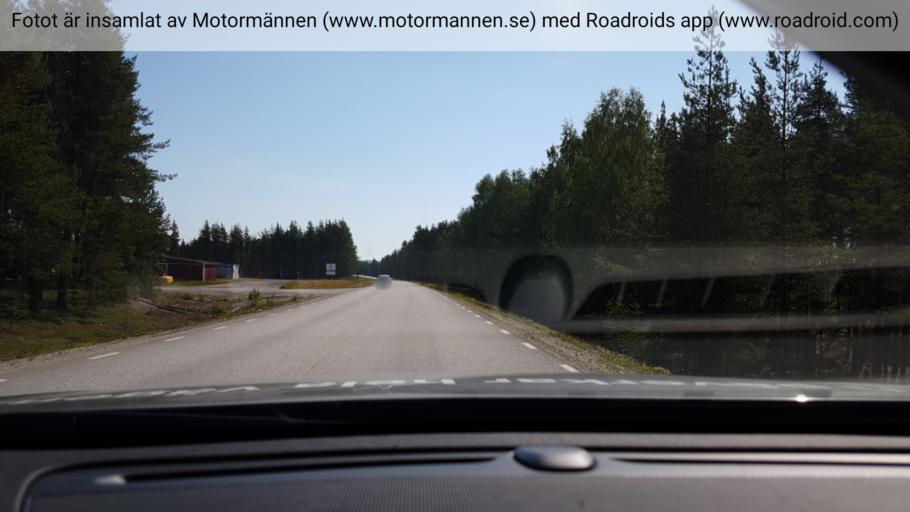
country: SE
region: Vaesterbotten
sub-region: Vindelns Kommun
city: Vindeln
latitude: 64.3258
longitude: 19.5294
